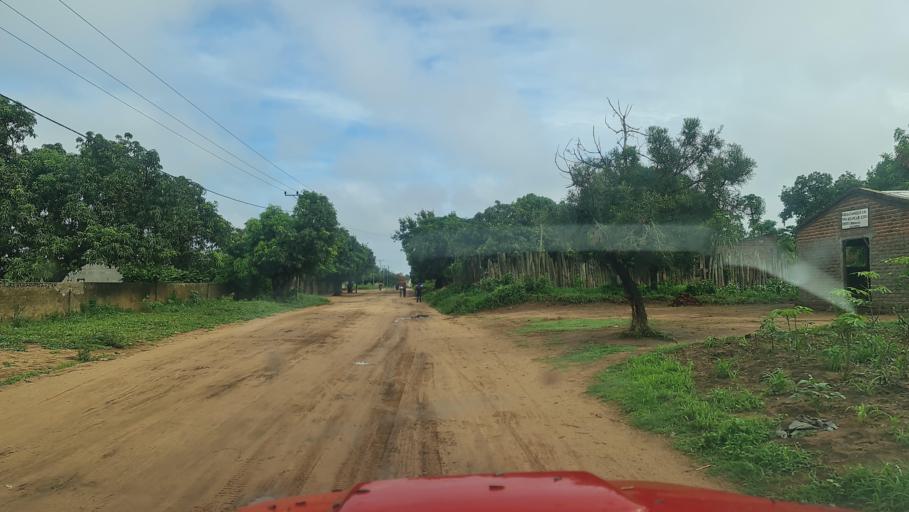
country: MW
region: Southern Region
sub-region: Nsanje District
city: Nsanje
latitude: -17.3201
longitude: 35.5920
